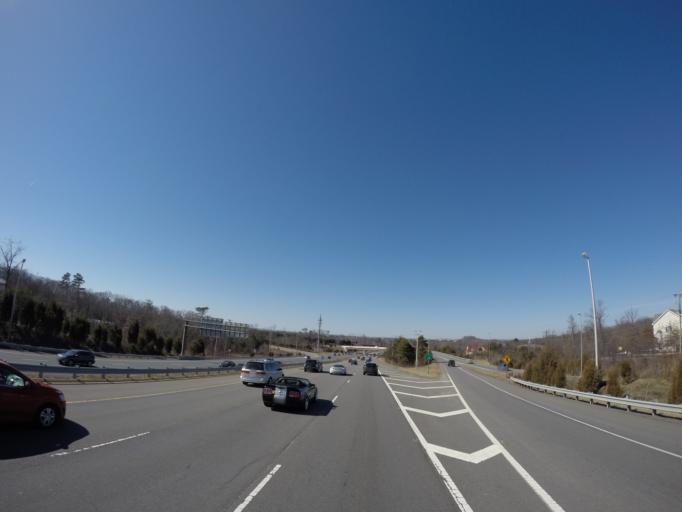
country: US
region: Virginia
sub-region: Loudoun County
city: Dulles Town Center
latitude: 39.0429
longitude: -77.4255
